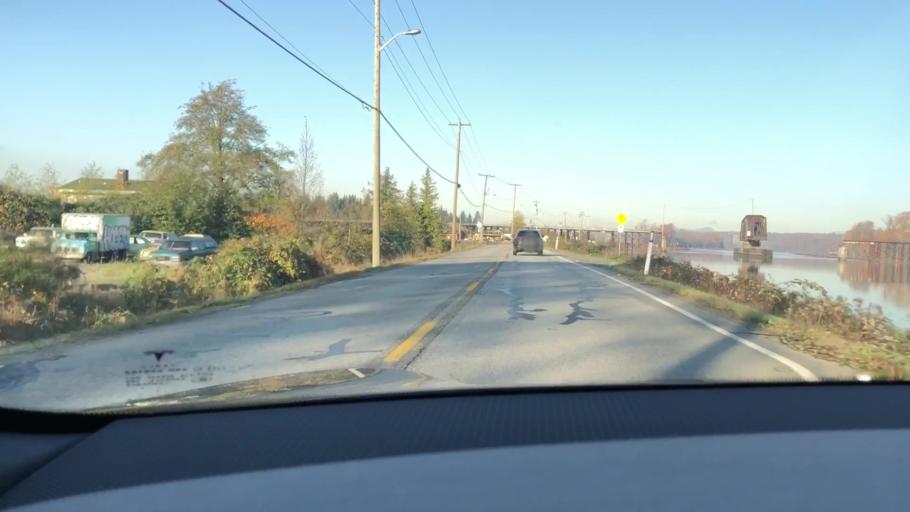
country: CA
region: British Columbia
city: New Westminster
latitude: 49.1802
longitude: -122.9834
